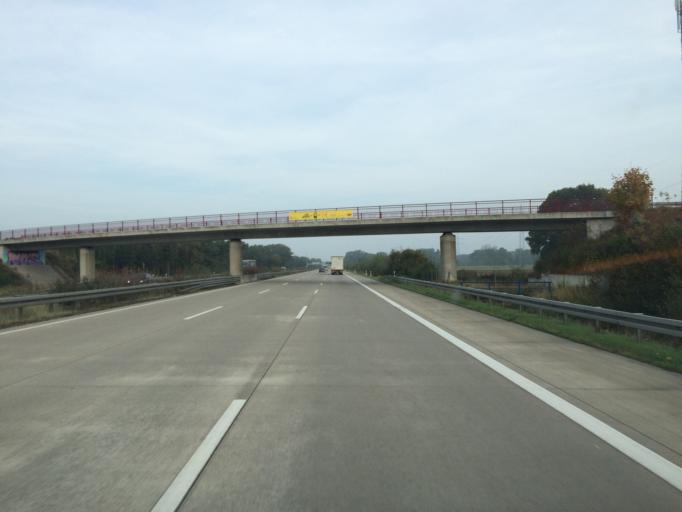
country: DE
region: Lower Saxony
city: Isernhagen Farster Bauerschaft
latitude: 52.5320
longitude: 9.8086
